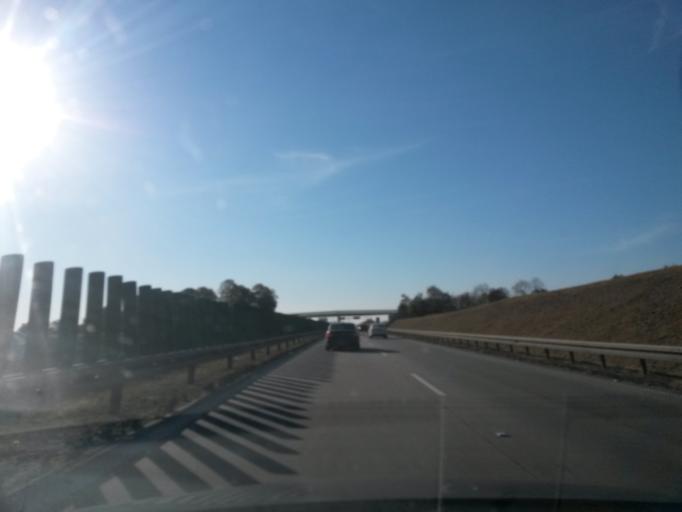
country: PL
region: Lower Silesian Voivodeship
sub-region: Powiat wroclawski
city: Katy Wroclawskie
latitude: 51.0197
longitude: 16.7391
